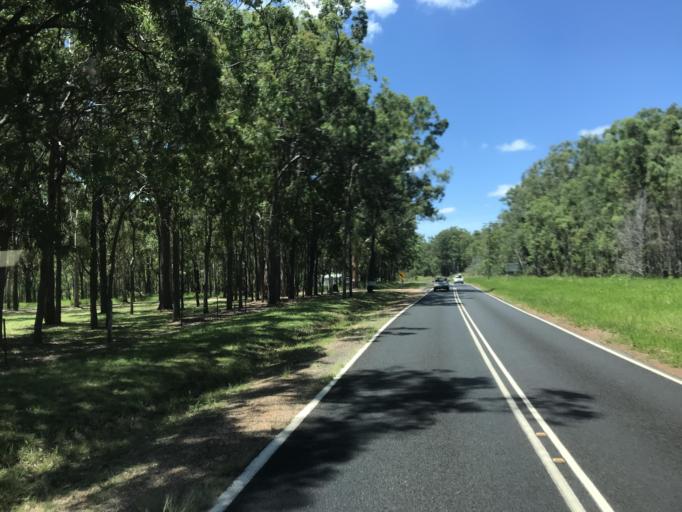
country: AU
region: Queensland
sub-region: Tablelands
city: Atherton
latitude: -17.4283
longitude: 145.3987
